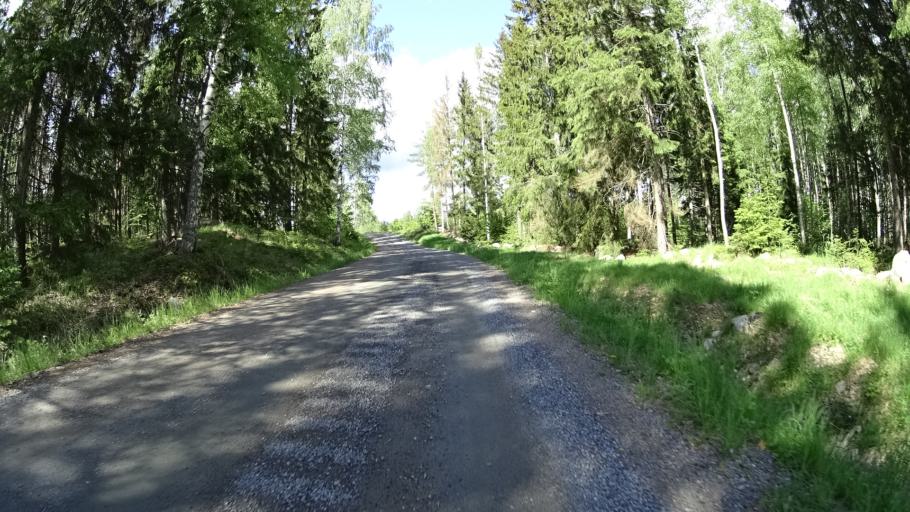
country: FI
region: Uusimaa
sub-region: Raaseporin
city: Pohja
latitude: 60.1786
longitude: 23.5876
